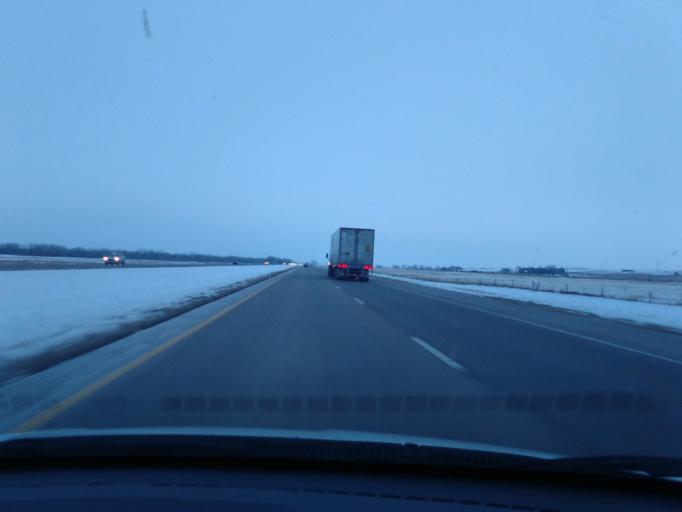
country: US
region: Nebraska
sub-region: Lincoln County
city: Sutherland
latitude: 41.1140
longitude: -101.3247
